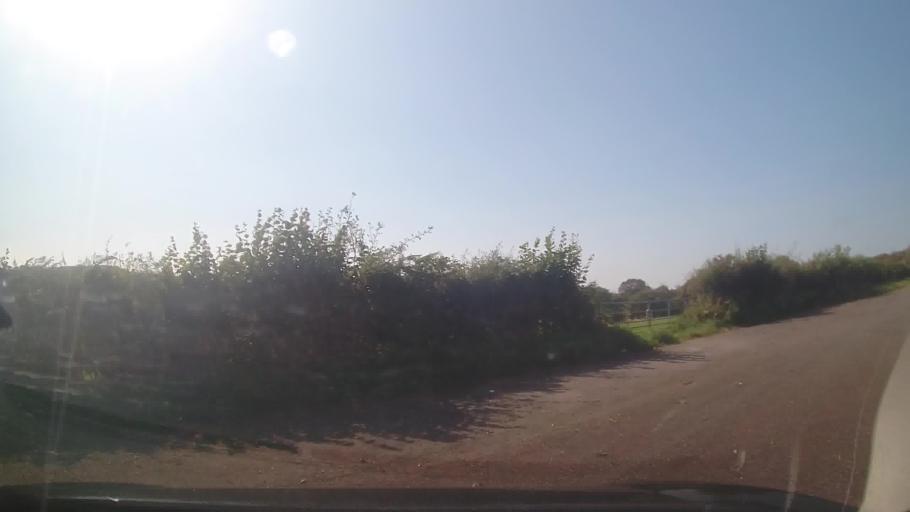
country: GB
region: Wales
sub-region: Carmarthenshire
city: Llanddowror
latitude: 51.8239
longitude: -4.5699
